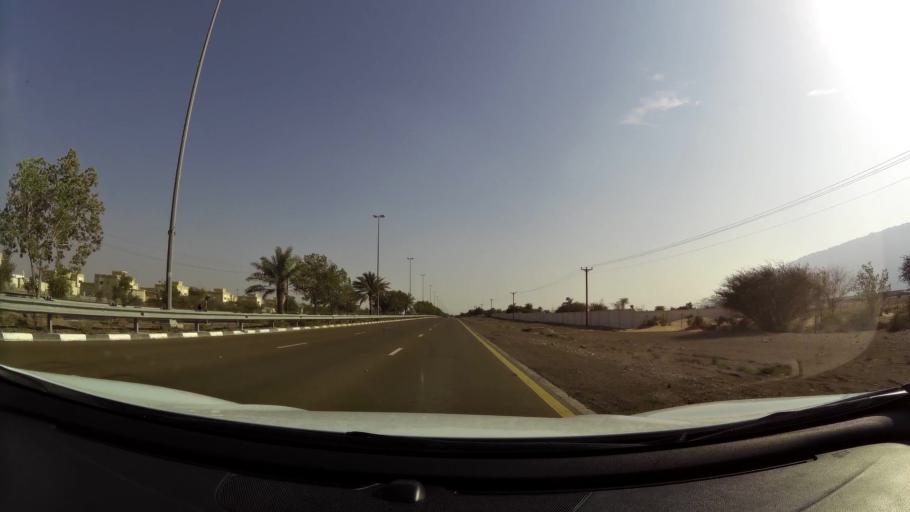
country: AE
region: Abu Dhabi
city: Al Ain
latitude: 24.0573
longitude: 55.8393
